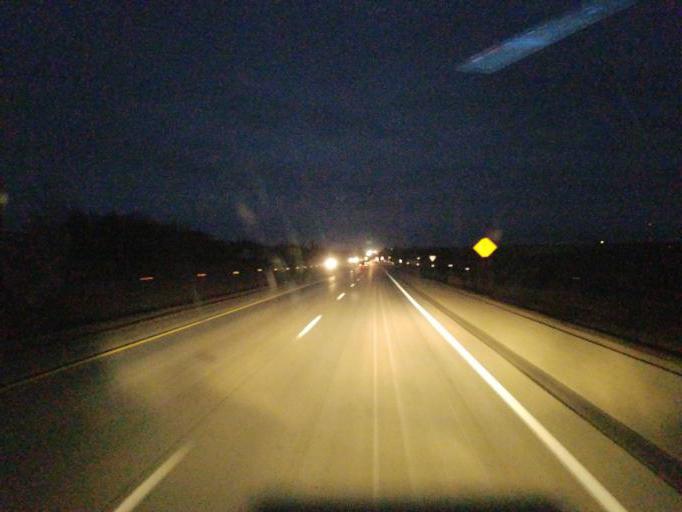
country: US
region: Iowa
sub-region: Guthrie County
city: Guthrie Center
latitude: 41.4960
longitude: -94.5182
